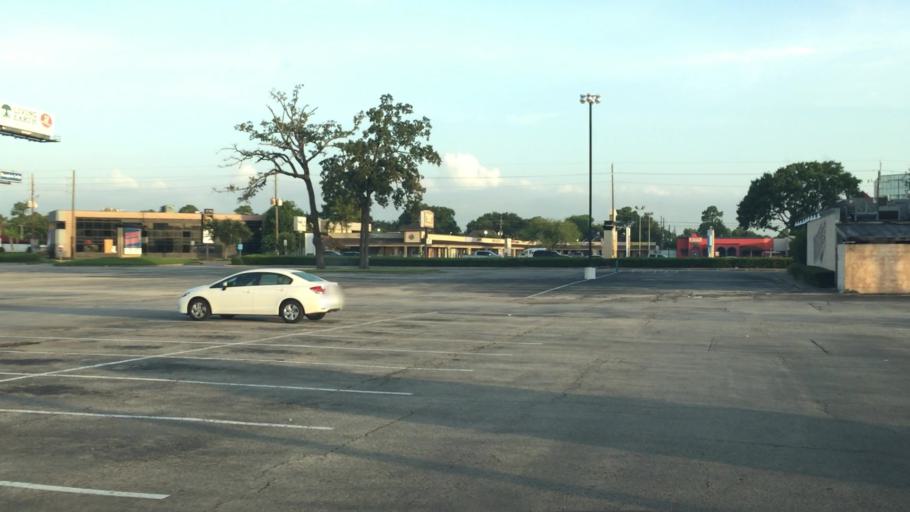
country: US
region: Texas
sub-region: Harris County
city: Hudson
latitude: 29.9856
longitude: -95.5000
